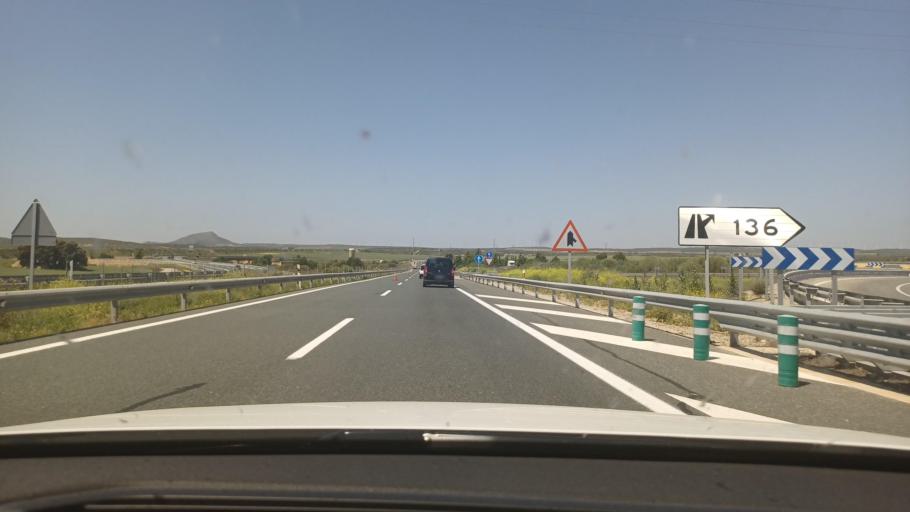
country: ES
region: Castille-La Mancha
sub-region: Provincia de Albacete
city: Alpera
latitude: 38.8789
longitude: -1.2212
